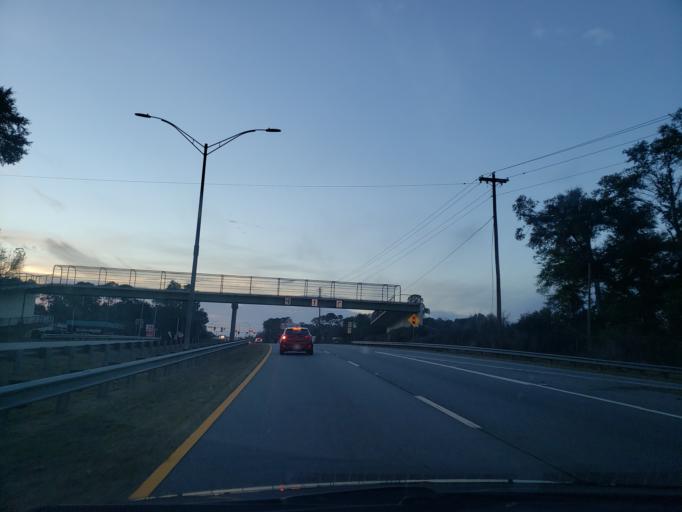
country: US
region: Georgia
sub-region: Dougherty County
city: Albany
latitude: 31.5725
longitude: -84.1154
